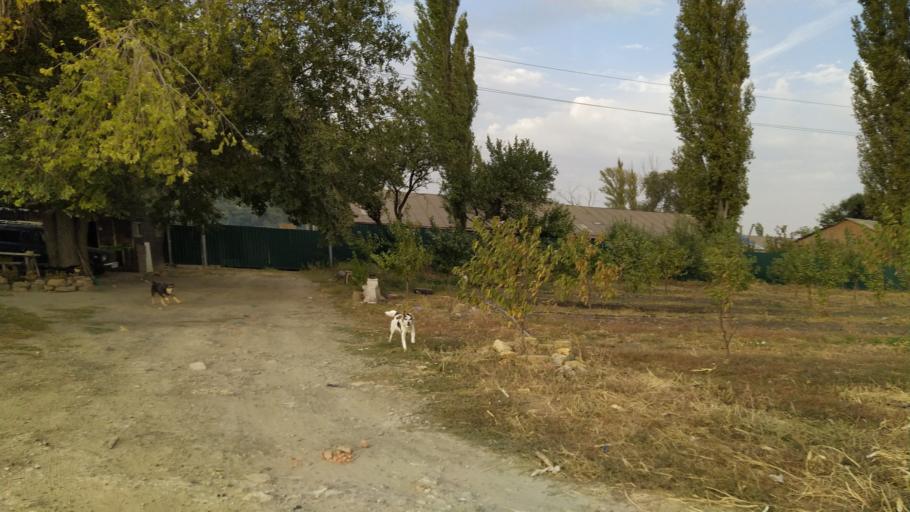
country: RU
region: Rostov
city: Kuleshovka
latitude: 47.1088
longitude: 39.6185
